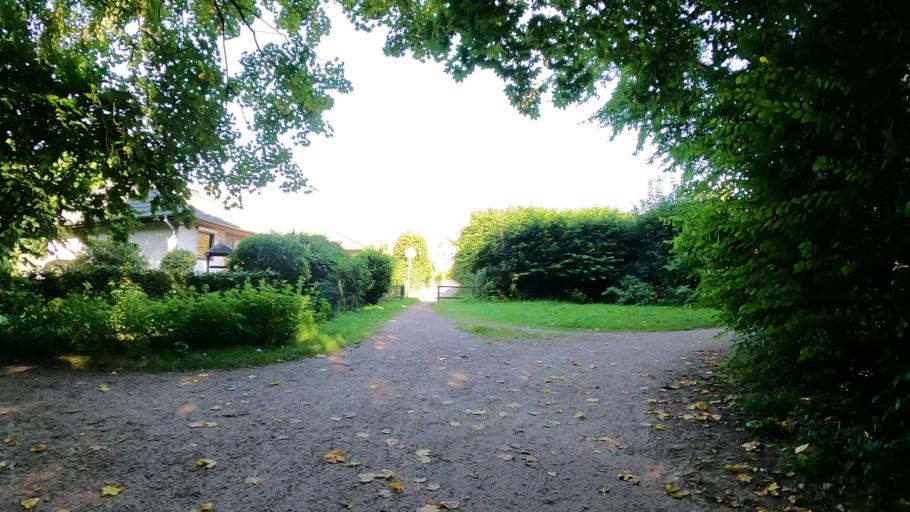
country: DE
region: Schleswig-Holstein
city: Henstedt-Ulzburg
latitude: 53.7849
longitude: 9.9813
